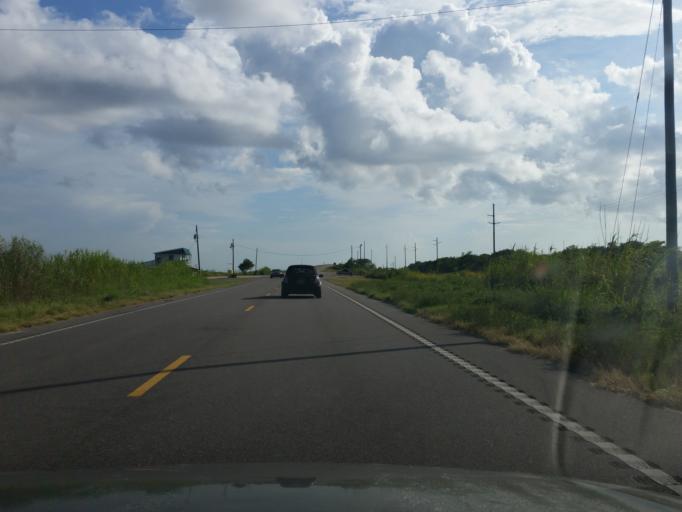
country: US
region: Alabama
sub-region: Mobile County
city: Dauphin Island
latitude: 30.3430
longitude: -88.1256
